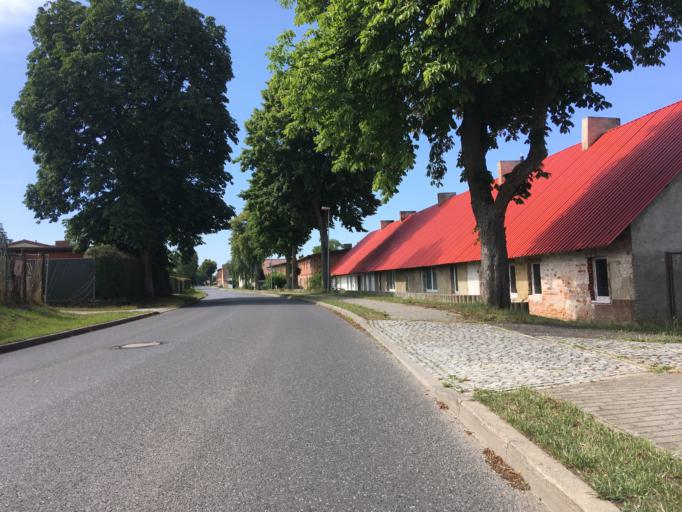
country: DE
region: Brandenburg
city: Zichow
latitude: 53.1916
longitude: 14.0389
